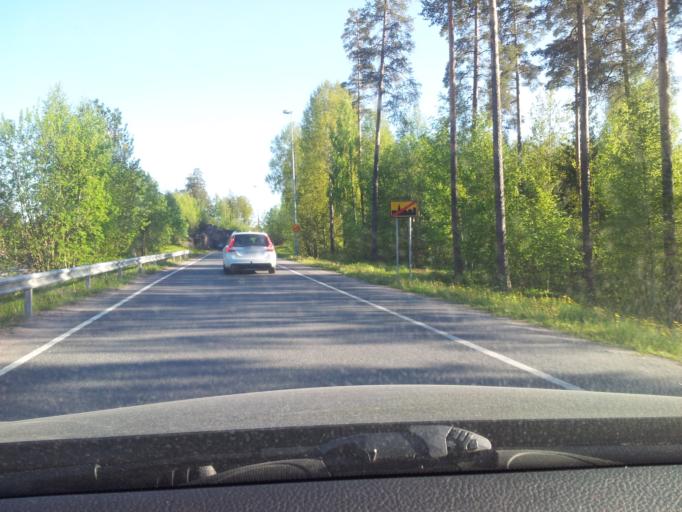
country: FI
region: Uusimaa
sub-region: Helsinki
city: Kauniainen
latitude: 60.2087
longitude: 24.7451
